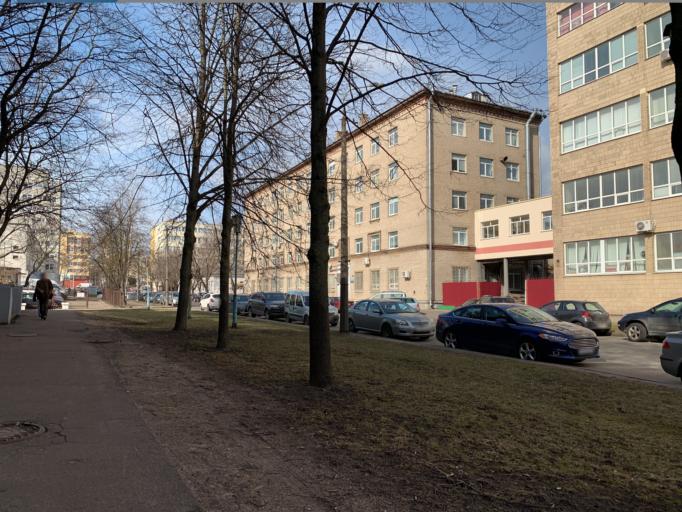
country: BY
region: Minsk
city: Minsk
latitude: 53.9115
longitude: 27.6030
